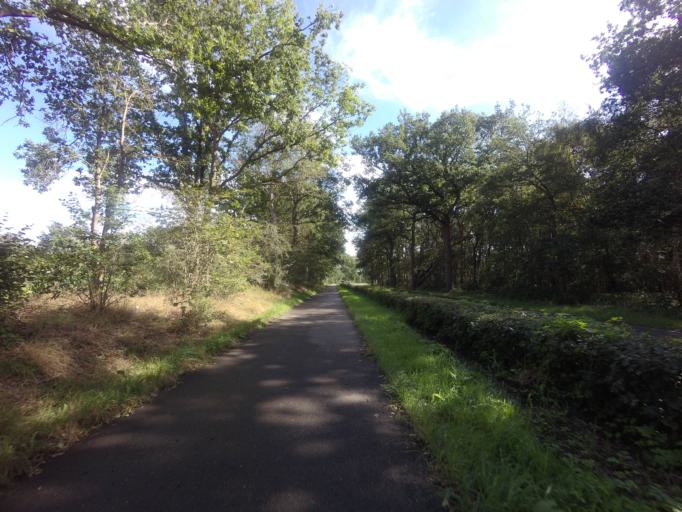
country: NL
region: Groningen
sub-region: Gemeente Leek
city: Leek
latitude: 53.0138
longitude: 6.2946
